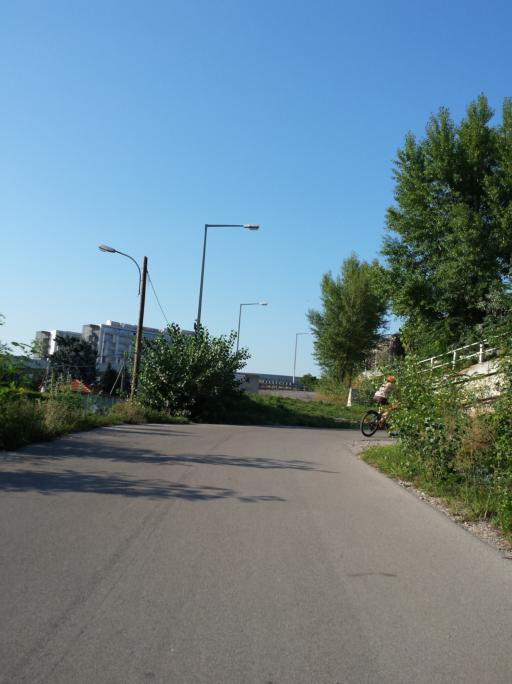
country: AT
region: Vienna
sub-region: Wien Stadt
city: Vienna
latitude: 48.2039
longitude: 16.4302
